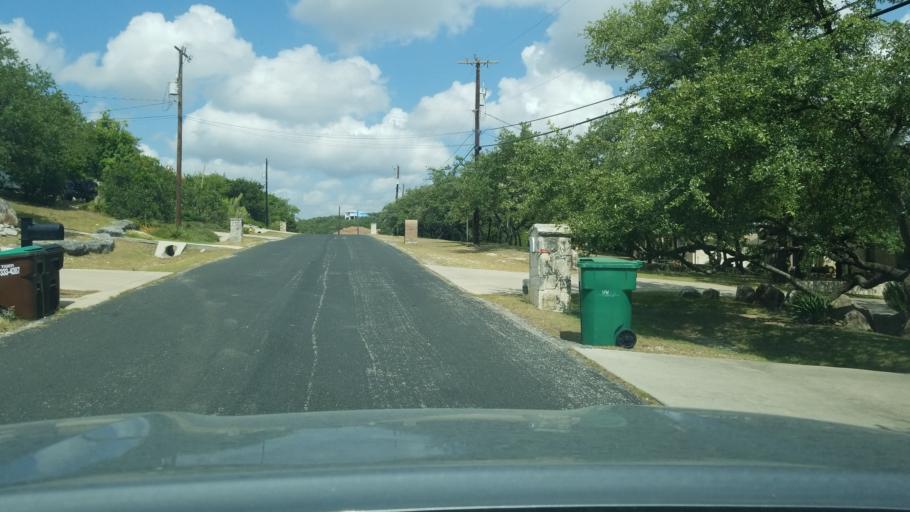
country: US
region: Texas
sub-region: Bexar County
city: Timberwood Park
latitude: 29.6838
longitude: -98.5113
